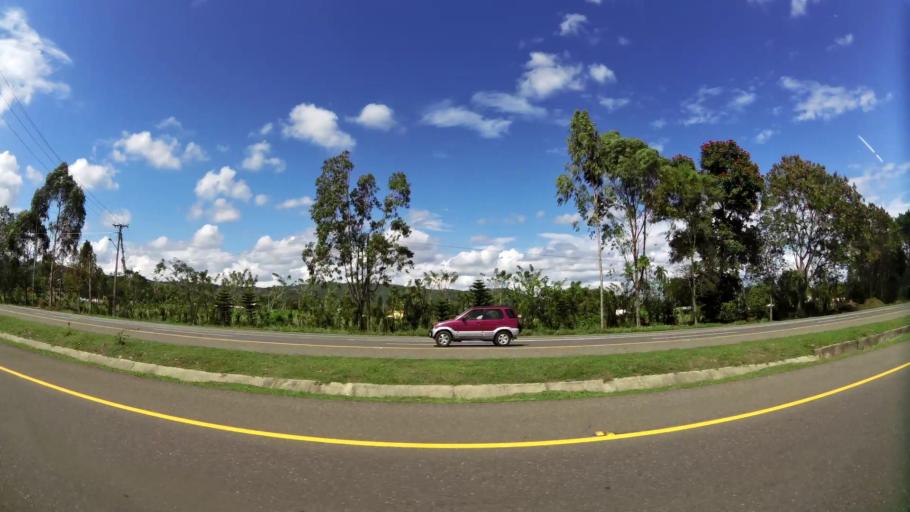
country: DO
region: La Vega
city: Concepcion de La Vega
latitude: 19.2485
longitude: -70.5499
